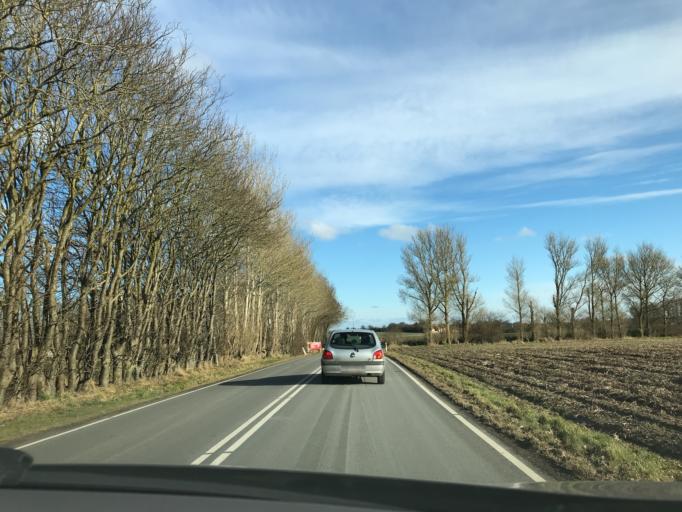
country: DK
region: South Denmark
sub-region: Nordfyns Kommune
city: Bogense
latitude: 55.5291
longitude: 10.0858
